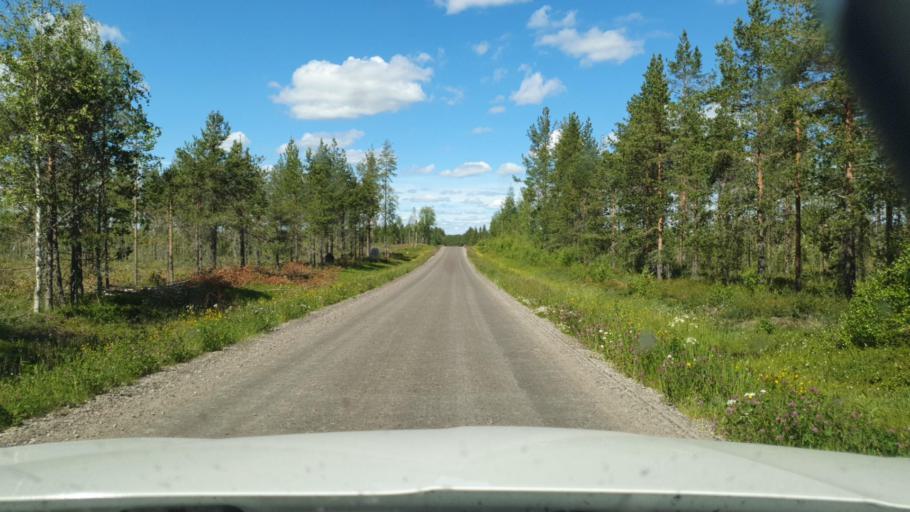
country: SE
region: Vaesterbotten
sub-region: Skelleftea Kommun
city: Byske
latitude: 65.1348
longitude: 21.1910
